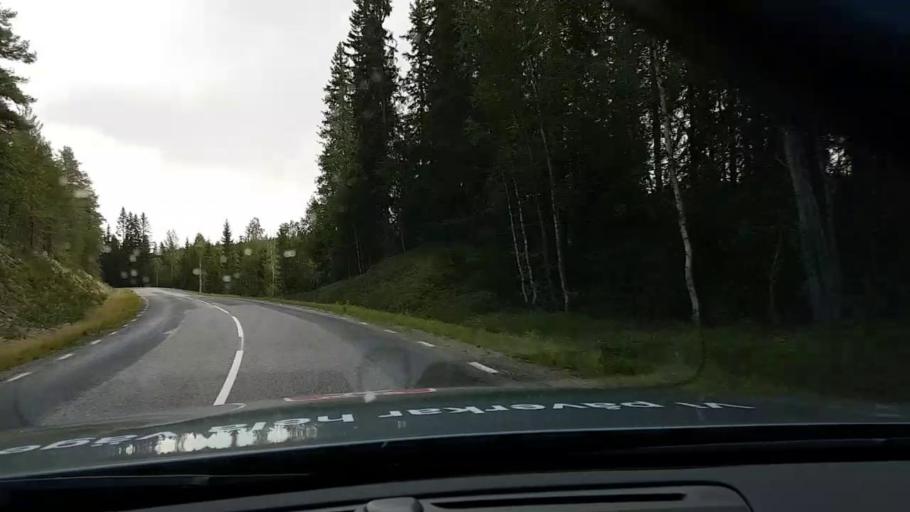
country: SE
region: Vaesterbotten
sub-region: Asele Kommun
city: Asele
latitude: 63.8376
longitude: 17.4346
